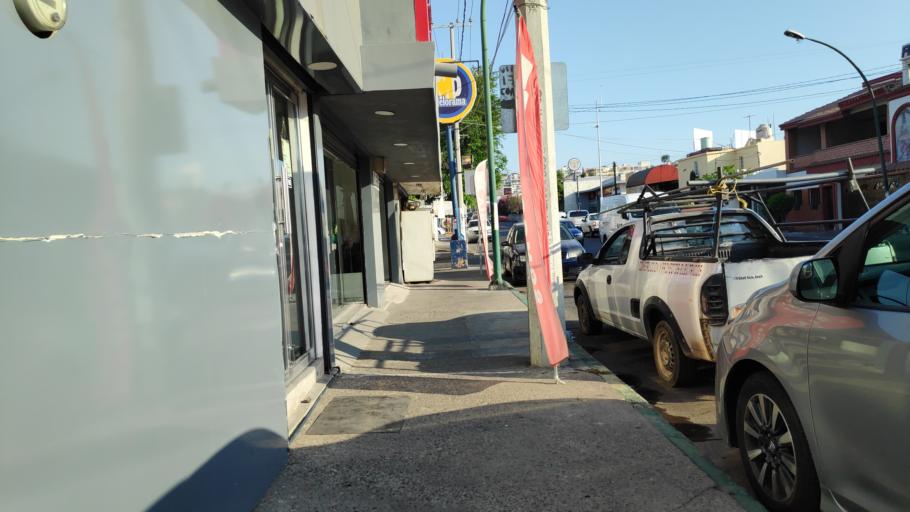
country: MX
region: Sinaloa
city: Culiacan
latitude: 24.7900
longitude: -107.4005
